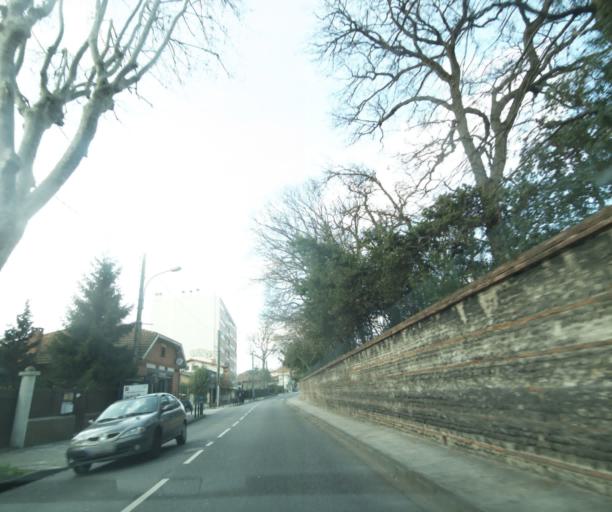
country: FR
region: Midi-Pyrenees
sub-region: Departement de la Haute-Garonne
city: Toulouse
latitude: 43.5897
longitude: 1.4708
